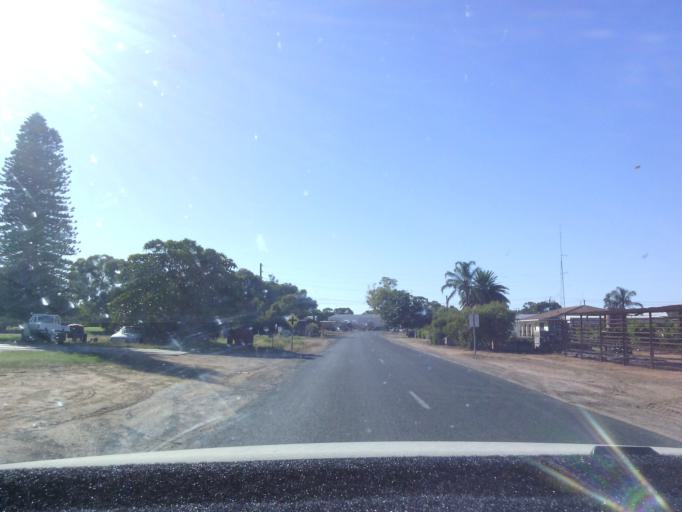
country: AU
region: South Australia
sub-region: Berri and Barmera
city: Berri
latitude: -34.2668
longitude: 140.6014
